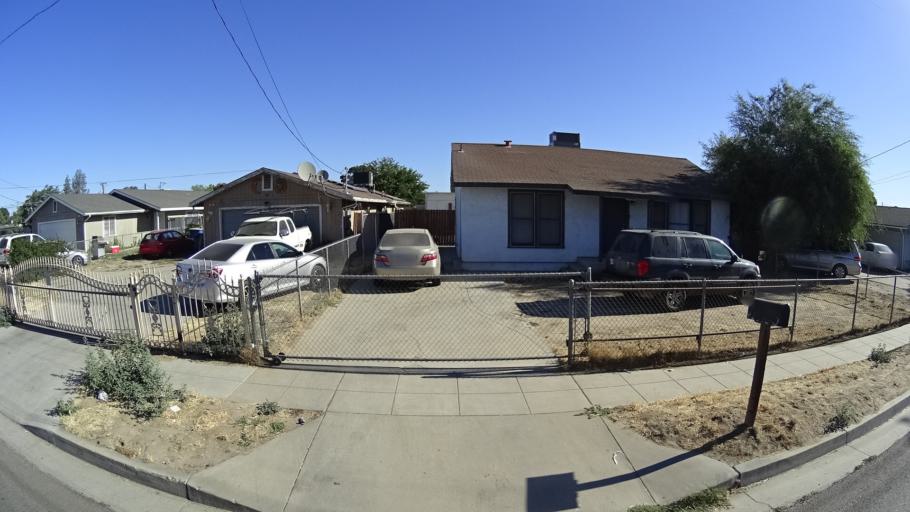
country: US
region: California
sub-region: Fresno County
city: Easton
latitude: 36.6923
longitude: -119.7990
